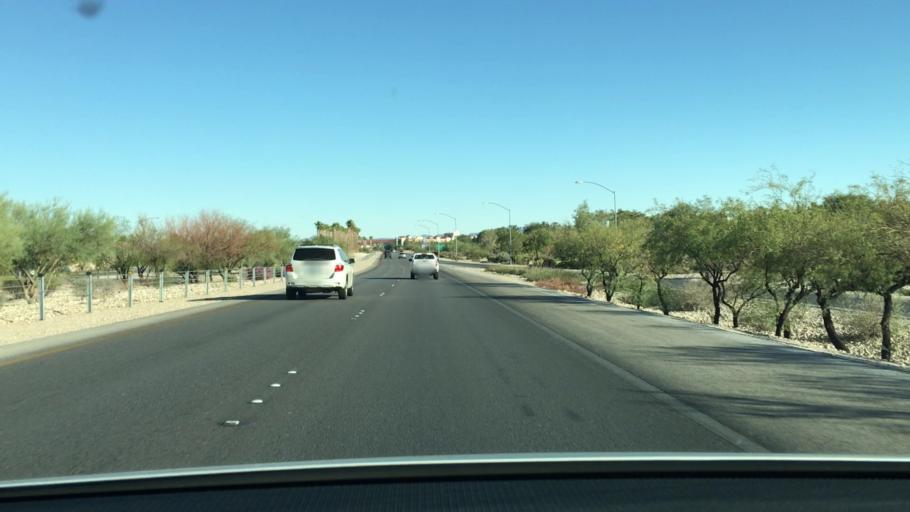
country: US
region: Nevada
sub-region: Clark County
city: Summerlin South
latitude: 36.1851
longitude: -115.3045
